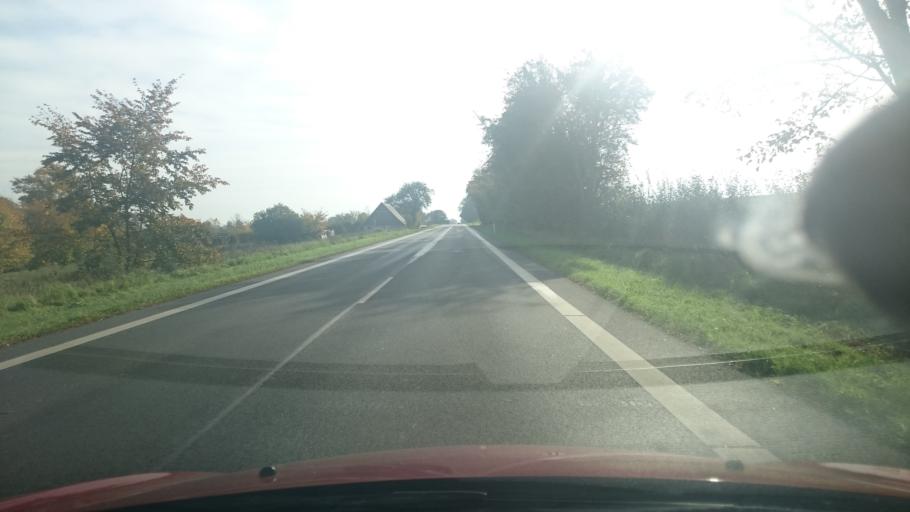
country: DK
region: Central Jutland
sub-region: Syddjurs Kommune
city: Hornslet
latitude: 56.3887
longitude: 10.2781
